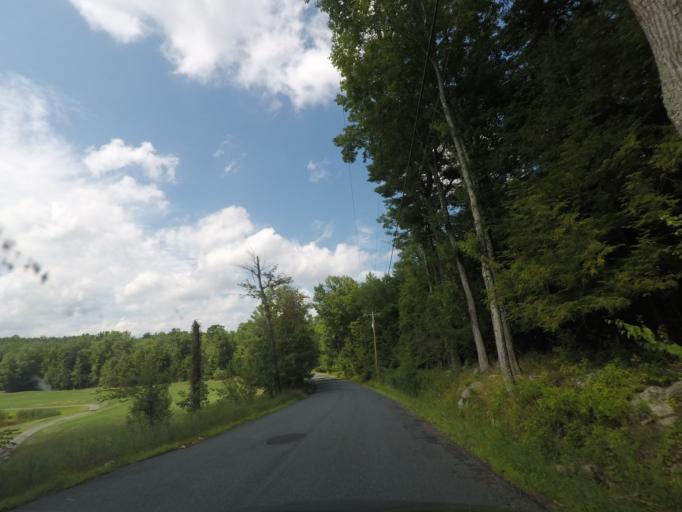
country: US
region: New York
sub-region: Rensselaer County
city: Averill Park
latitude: 42.5895
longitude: -73.5468
